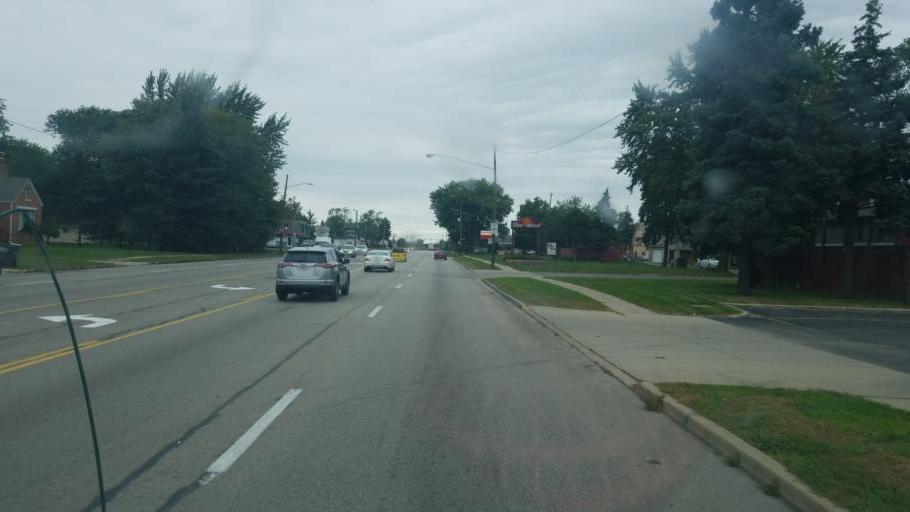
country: US
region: Ohio
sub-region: Lucas County
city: Holland
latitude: 41.6189
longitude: -83.6644
